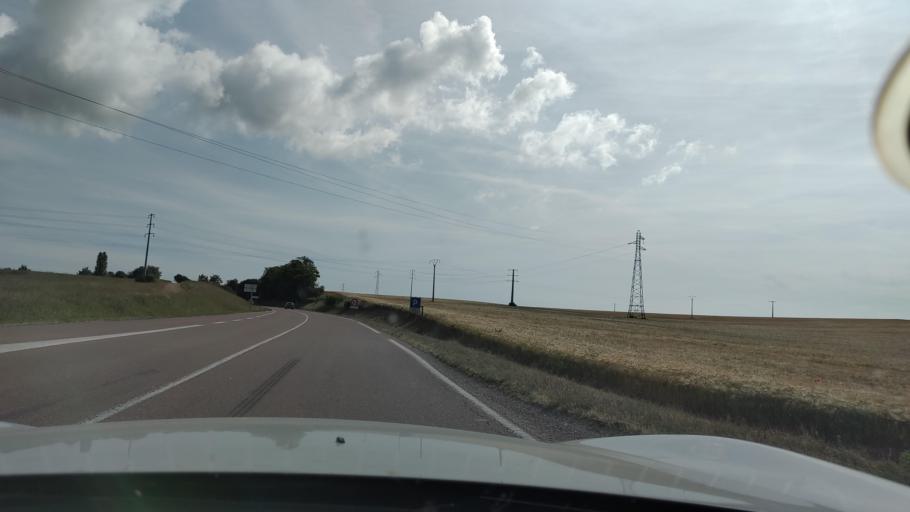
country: FR
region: Champagne-Ardenne
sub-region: Departement de l'Aube
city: Nogent-sur-Seine
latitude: 48.4848
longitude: 3.5151
